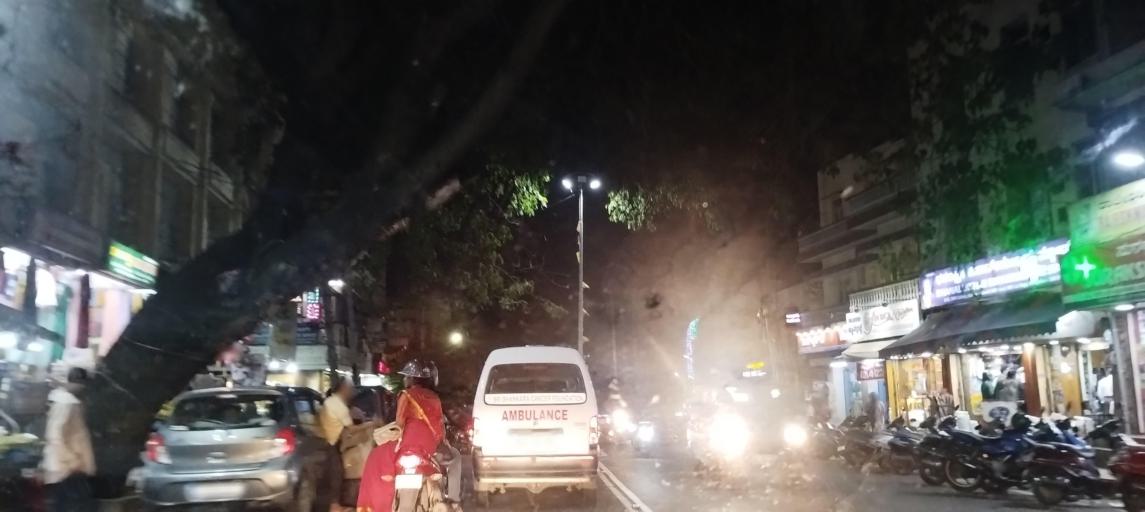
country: IN
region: Karnataka
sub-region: Bangalore Urban
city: Bangalore
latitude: 12.9387
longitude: 77.5533
